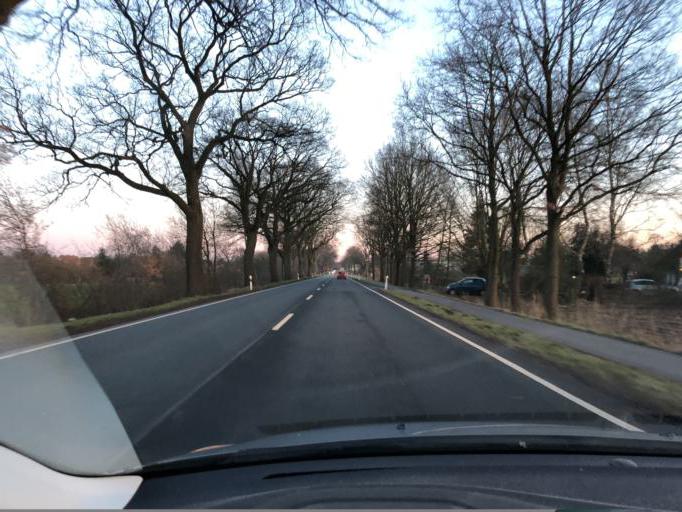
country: DE
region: Lower Saxony
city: Wietzen
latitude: 52.7157
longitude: 9.0636
